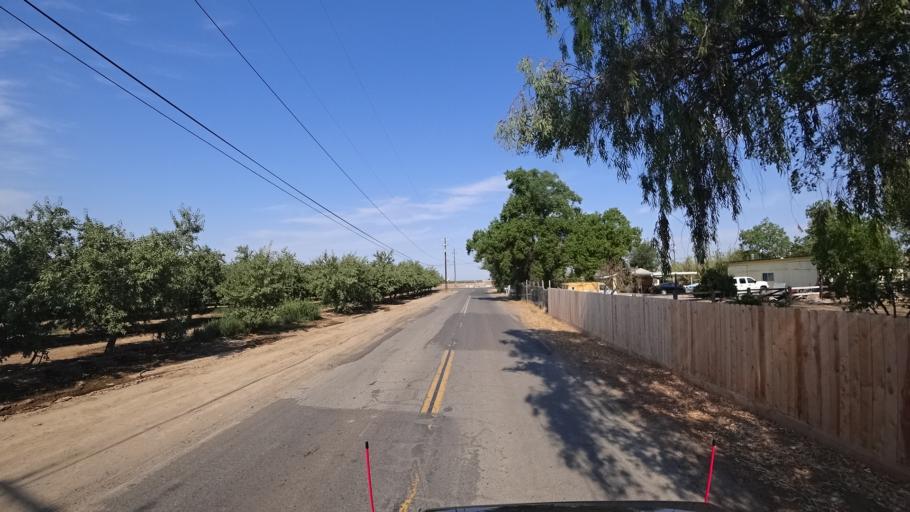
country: US
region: California
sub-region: Fresno County
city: West Park
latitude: 36.7427
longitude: -119.8611
